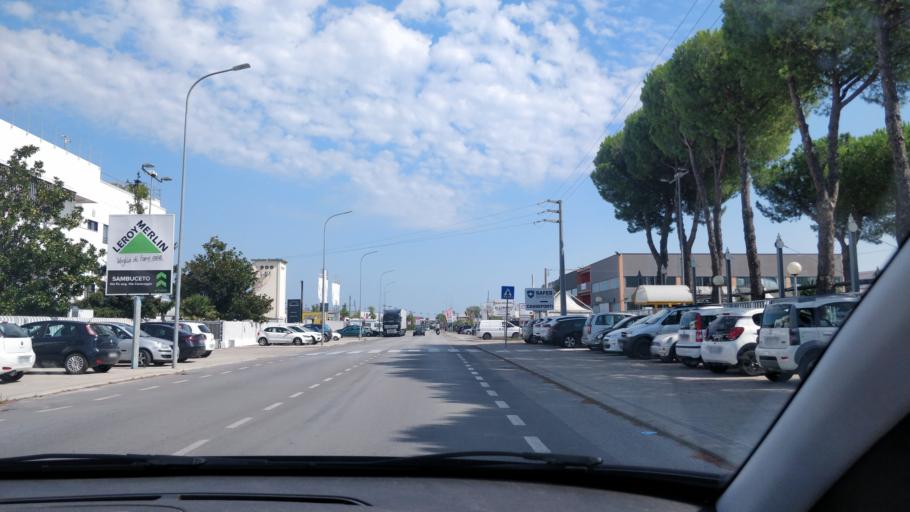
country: IT
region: Abruzzo
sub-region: Provincia di Pescara
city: Santa Teresa
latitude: 42.4120
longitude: 14.1678
